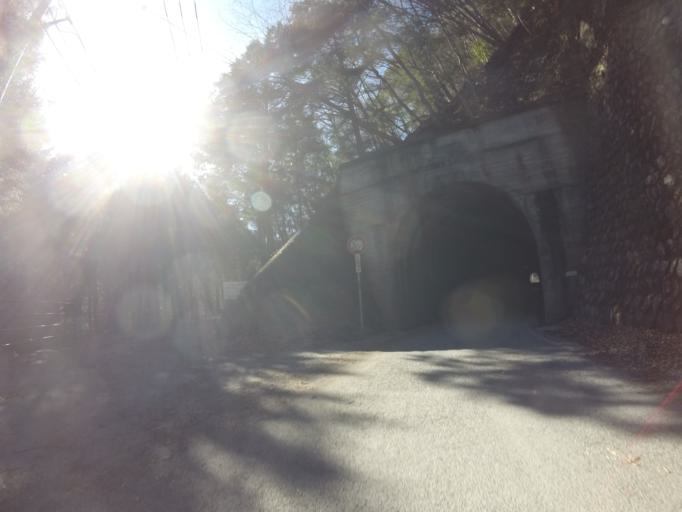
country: JP
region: Yamanashi
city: Ryuo
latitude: 35.4099
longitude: 138.3331
